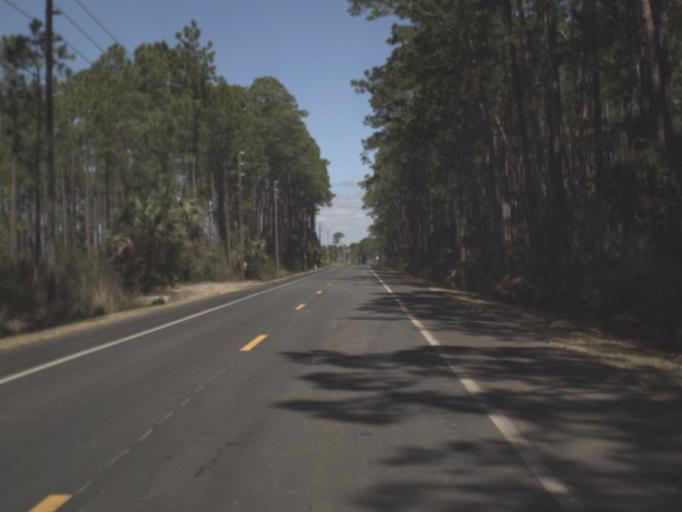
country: US
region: Florida
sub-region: Gulf County
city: Port Saint Joe
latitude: 29.7308
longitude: -85.3023
